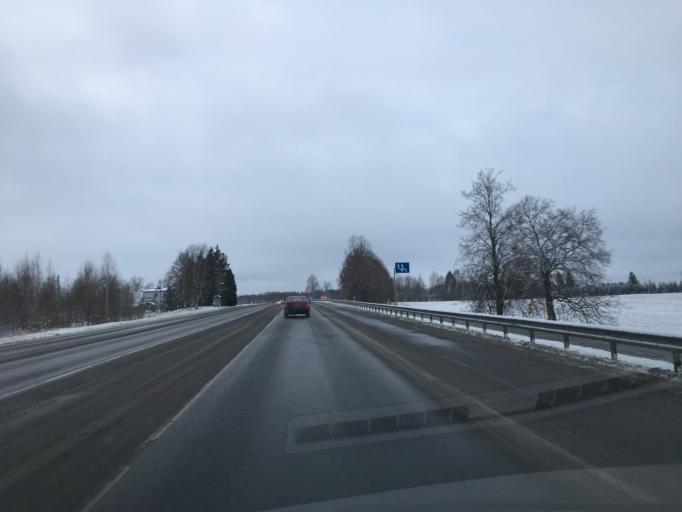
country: EE
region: Tartu
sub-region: UElenurme vald
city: Ulenurme
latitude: 58.3416
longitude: 26.6574
